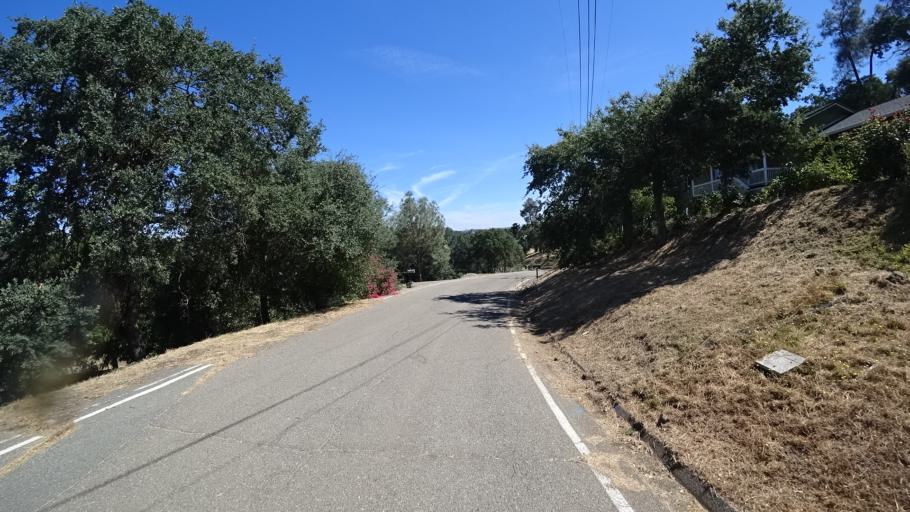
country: US
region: California
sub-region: Calaveras County
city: Rancho Calaveras
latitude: 38.1516
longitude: -120.8512
